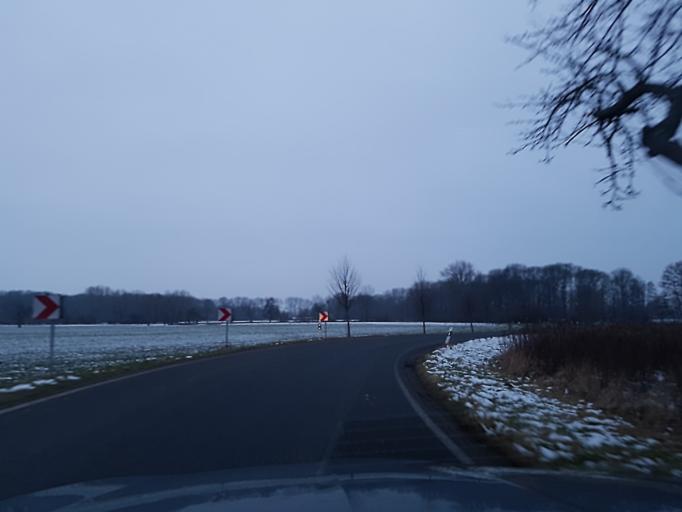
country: DE
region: Saxony
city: Stauchitz
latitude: 51.2522
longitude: 13.2073
